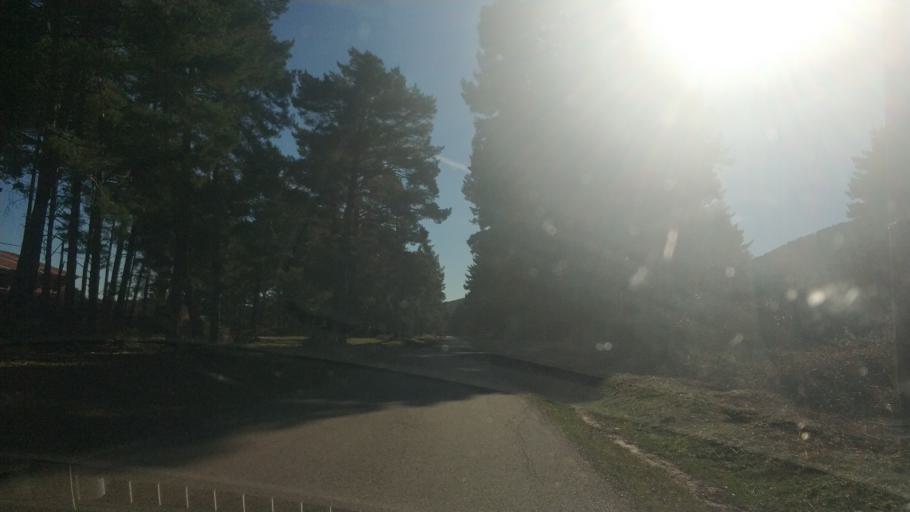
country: ES
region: Castille and Leon
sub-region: Provincia de Soria
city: Vinuesa
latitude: 41.9402
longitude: -2.7794
